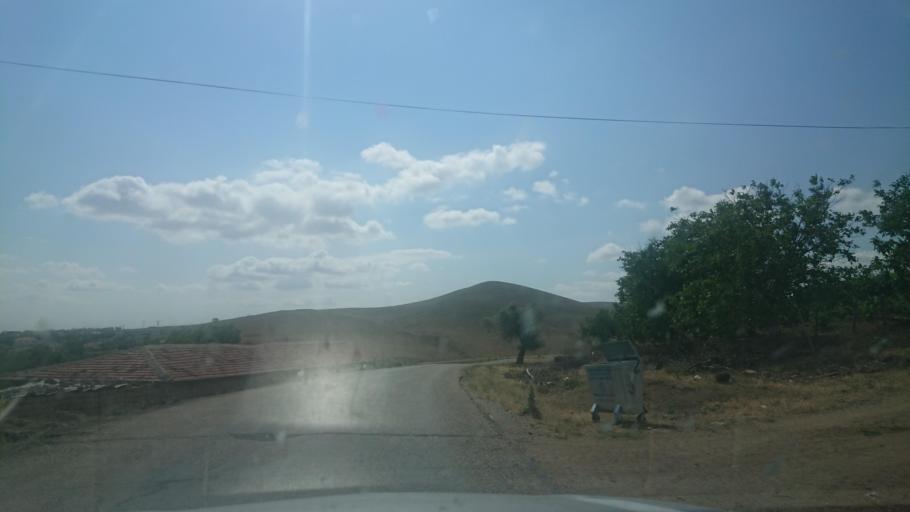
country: TR
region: Aksaray
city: Sariyahsi
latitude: 39.0116
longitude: 33.9459
